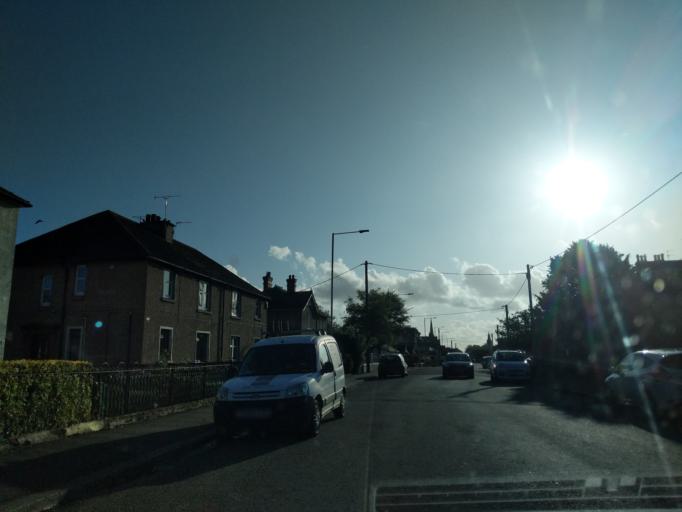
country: GB
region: Scotland
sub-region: Dumfries and Galloway
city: Kirkcudbright
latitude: 54.8416
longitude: -4.0436
